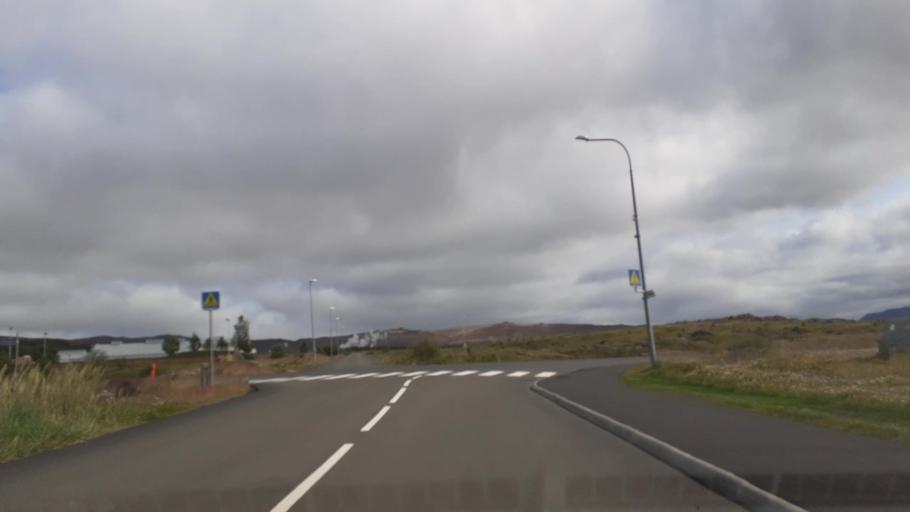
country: IS
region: Northeast
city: Laugar
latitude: 65.6419
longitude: -16.8965
